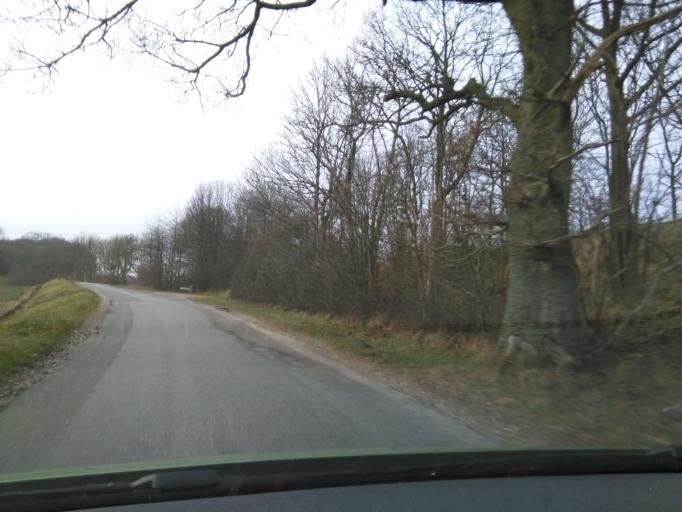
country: DK
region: Central Jutland
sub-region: Odder Kommune
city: Odder
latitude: 55.9304
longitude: 10.0935
